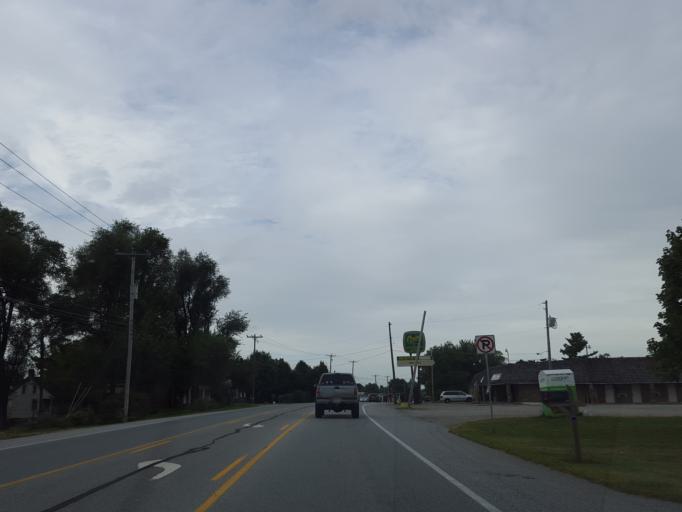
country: US
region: Pennsylvania
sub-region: Adams County
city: Abbottstown
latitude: 39.8972
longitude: -76.9535
